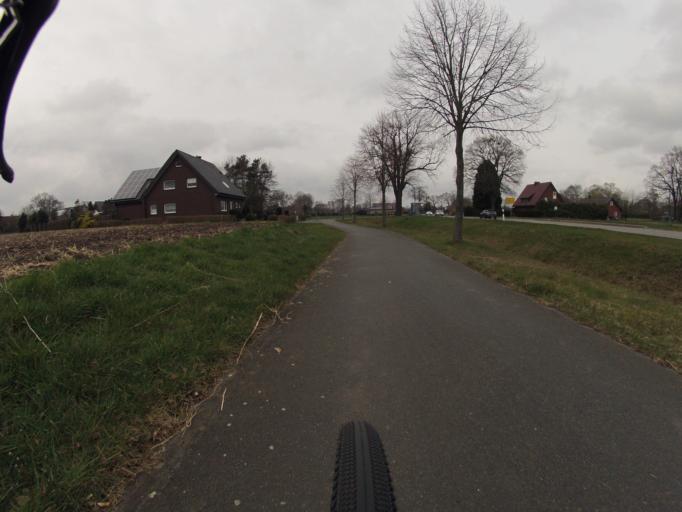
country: DE
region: North Rhine-Westphalia
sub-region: Regierungsbezirk Munster
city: Recke
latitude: 52.3500
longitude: 7.7276
